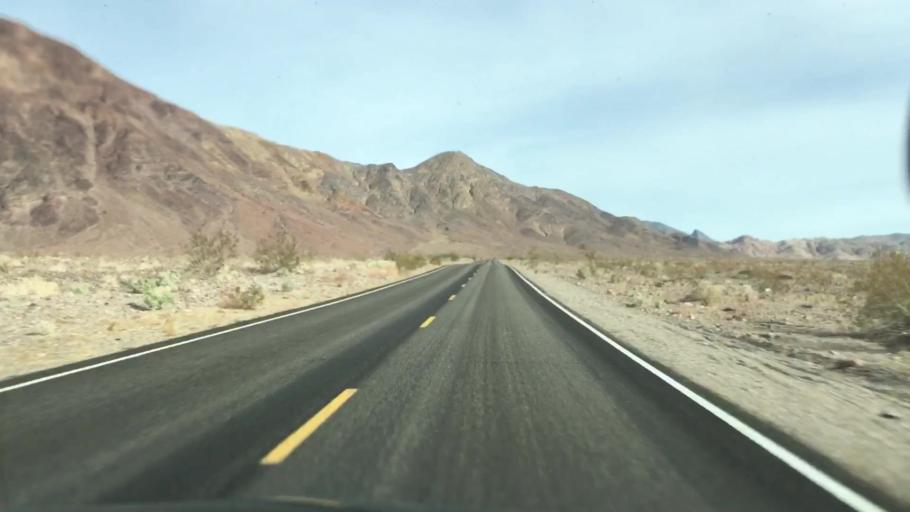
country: US
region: Nevada
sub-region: Nye County
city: Beatty
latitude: 36.6950
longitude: -117.0012
